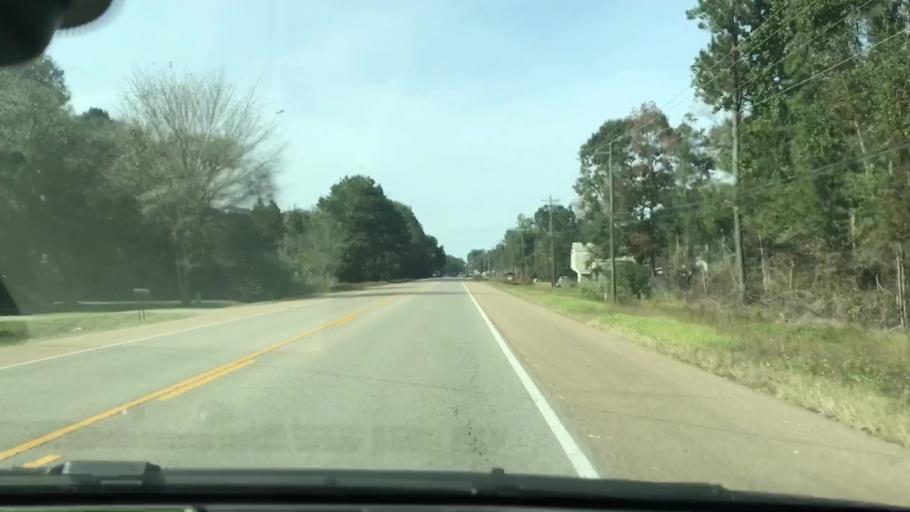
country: US
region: Louisiana
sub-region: Saint Tammany Parish
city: Pearl River
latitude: 30.4080
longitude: -89.7739
